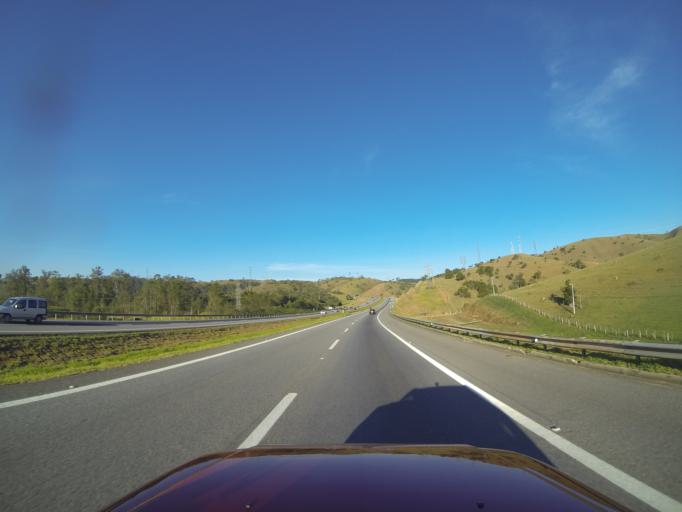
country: BR
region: Sao Paulo
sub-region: Jacarei
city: Jacarei
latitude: -23.3421
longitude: -45.9659
